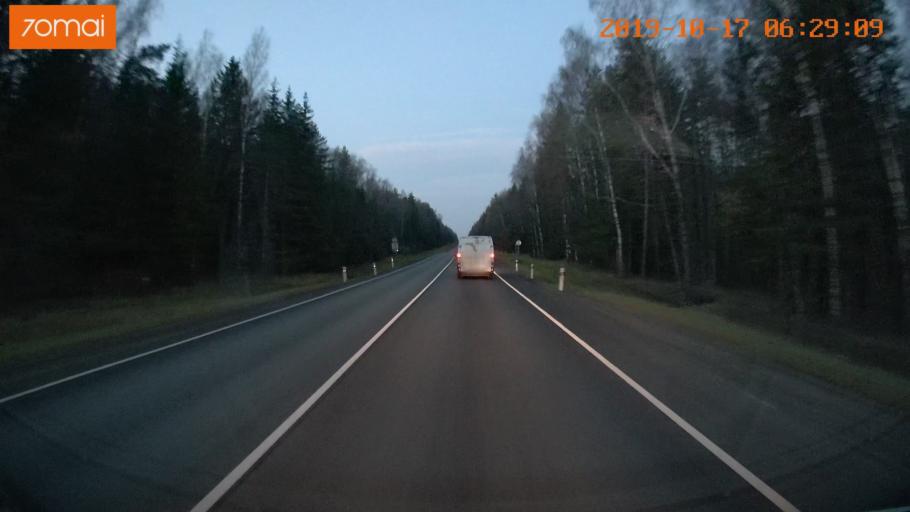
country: RU
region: Ivanovo
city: Lezhnevo
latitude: 56.7476
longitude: 40.7500
